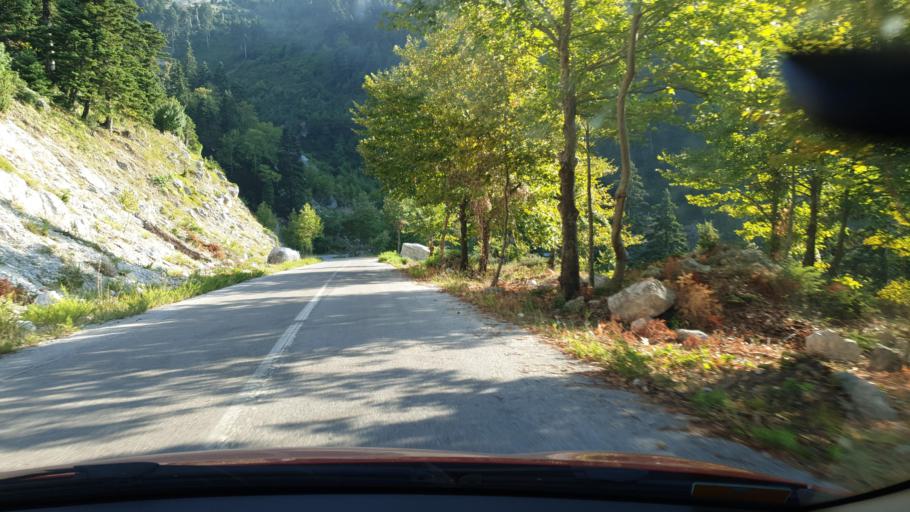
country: GR
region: Central Greece
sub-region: Nomos Evvoias
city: Yimnon
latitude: 38.5951
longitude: 23.9061
